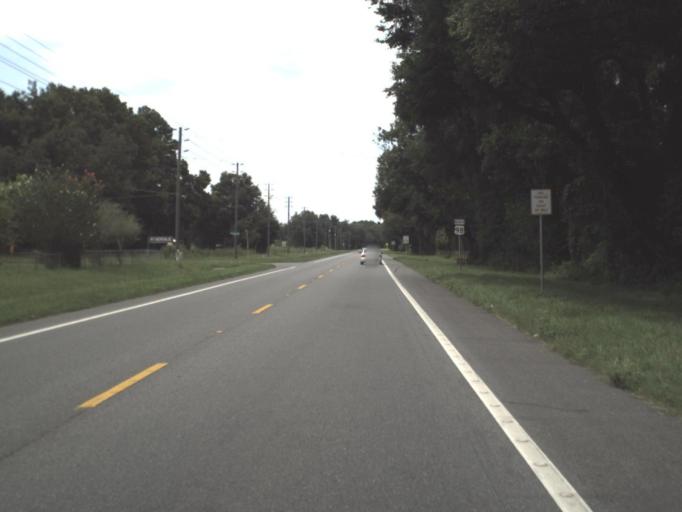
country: US
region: Florida
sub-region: Pasco County
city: Lacoochee
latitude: 28.4789
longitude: -82.1960
